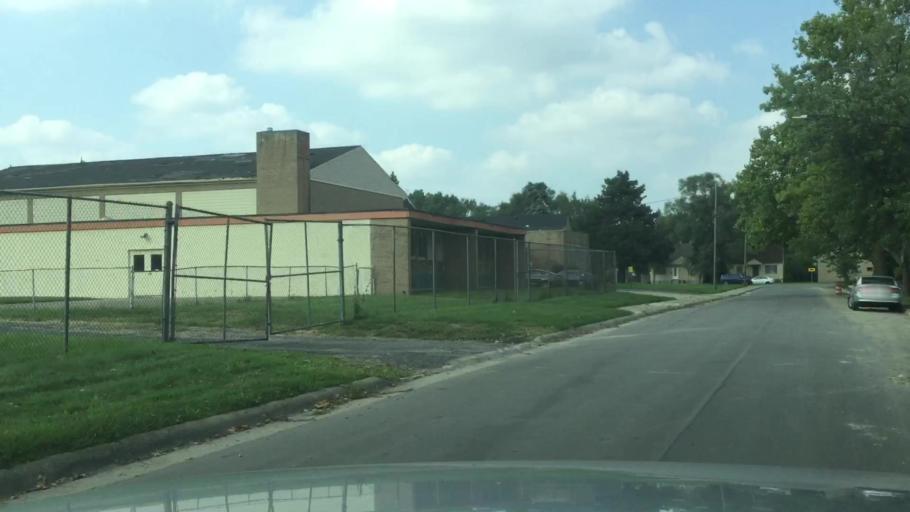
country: US
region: Michigan
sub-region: Wayne County
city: Dearborn
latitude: 42.3640
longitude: -83.2004
